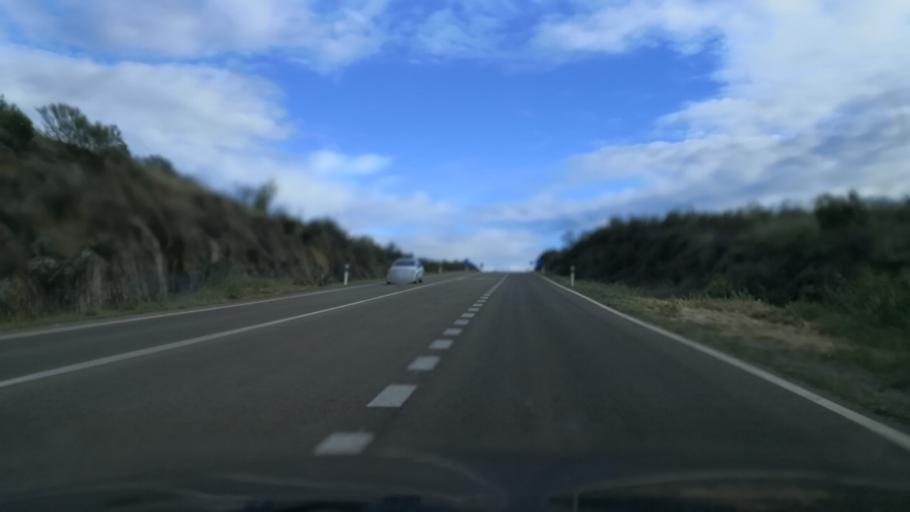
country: ES
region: Extremadura
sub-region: Provincia de Caceres
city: Coria
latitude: 39.9479
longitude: -6.5086
